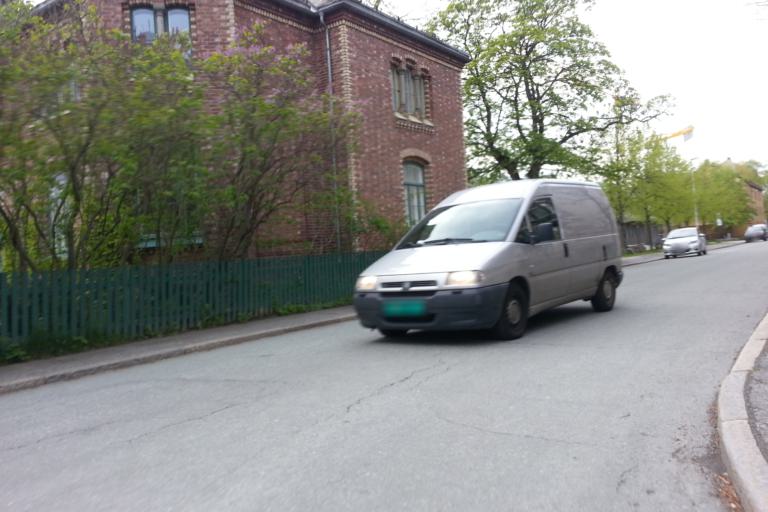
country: NO
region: Sor-Trondelag
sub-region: Trondheim
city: Trondheim
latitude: 63.4265
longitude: 10.3898
